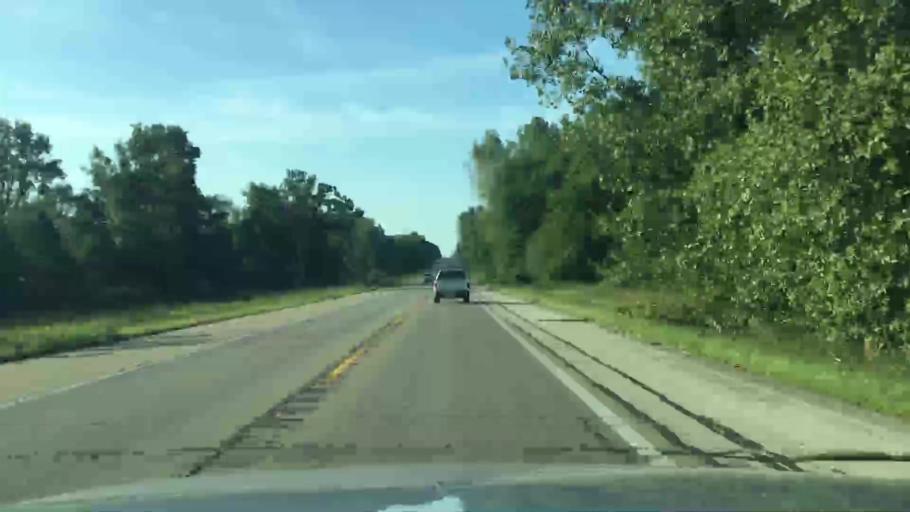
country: US
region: Michigan
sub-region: Jackson County
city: Vandercook Lake
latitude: 42.0968
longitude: -84.3639
